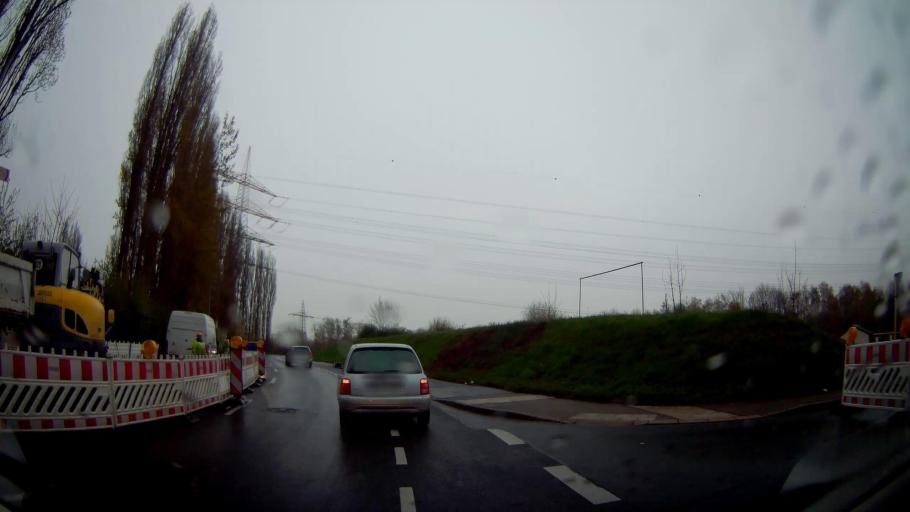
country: DE
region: North Rhine-Westphalia
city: Castrop-Rauxel
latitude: 51.5214
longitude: 7.3764
